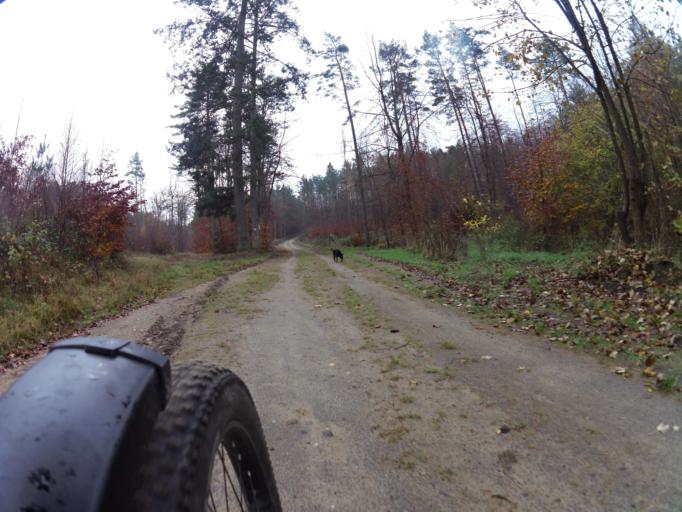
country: PL
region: Pomeranian Voivodeship
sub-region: Powiat pucki
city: Krokowa
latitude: 54.7792
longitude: 18.0917
